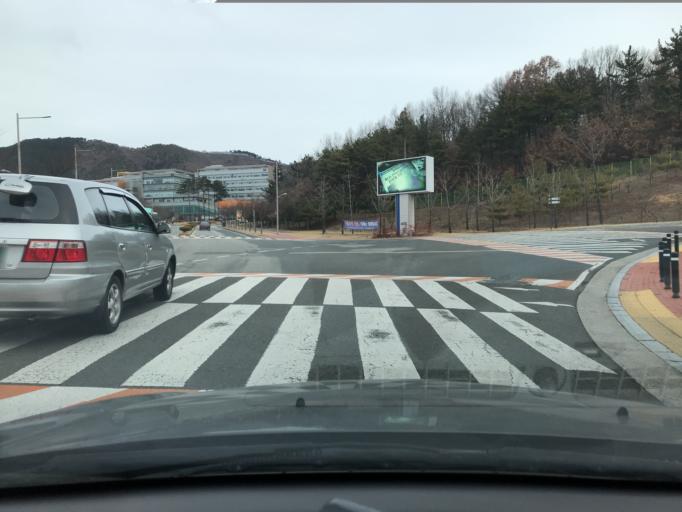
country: KR
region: Daegu
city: Hwawon
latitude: 35.7012
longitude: 128.4586
